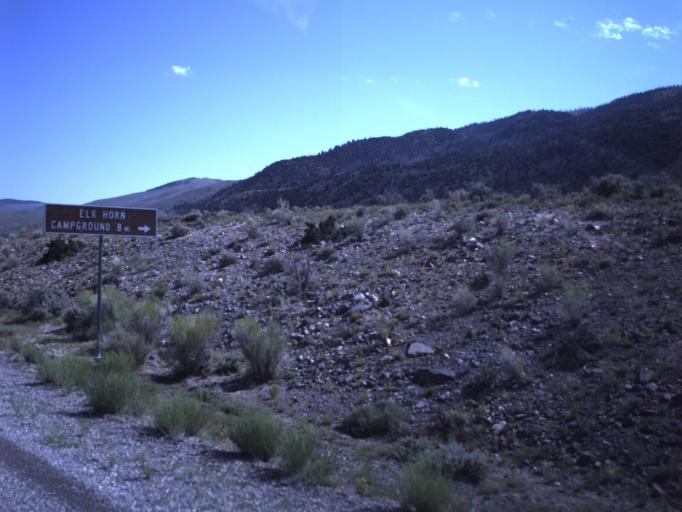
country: US
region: Utah
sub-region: Wayne County
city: Loa
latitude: 38.5107
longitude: -111.5260
